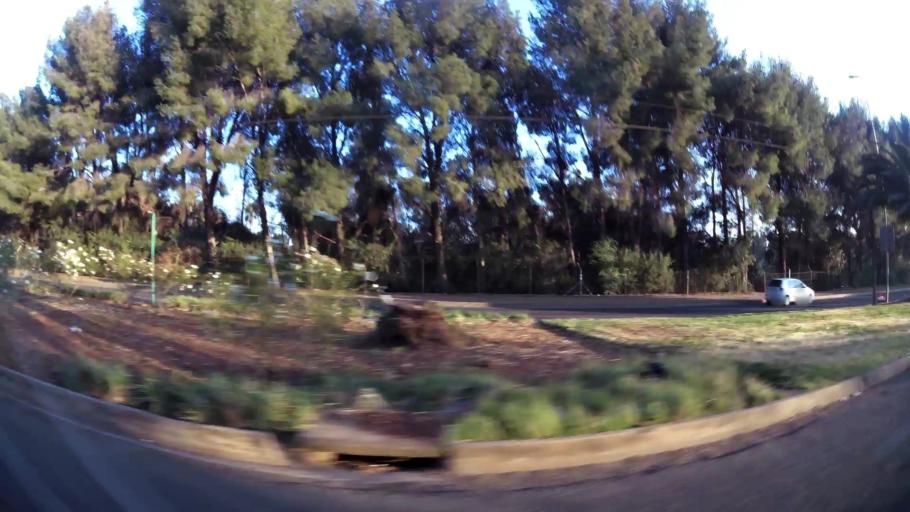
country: ZA
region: Orange Free State
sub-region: Mangaung Metropolitan Municipality
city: Bloemfontein
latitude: -29.0852
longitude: 26.1560
